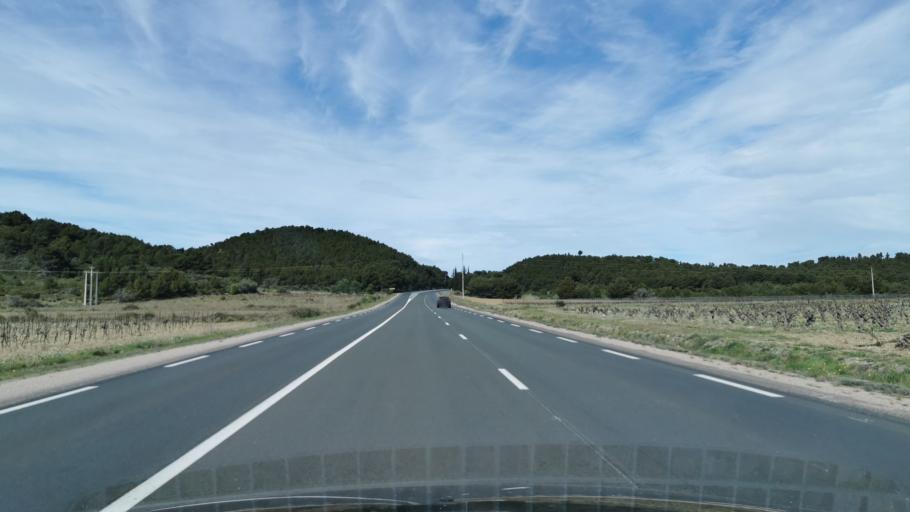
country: FR
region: Languedoc-Roussillon
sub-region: Departement de l'Aude
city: Sigean
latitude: 43.0040
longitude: 2.9694
